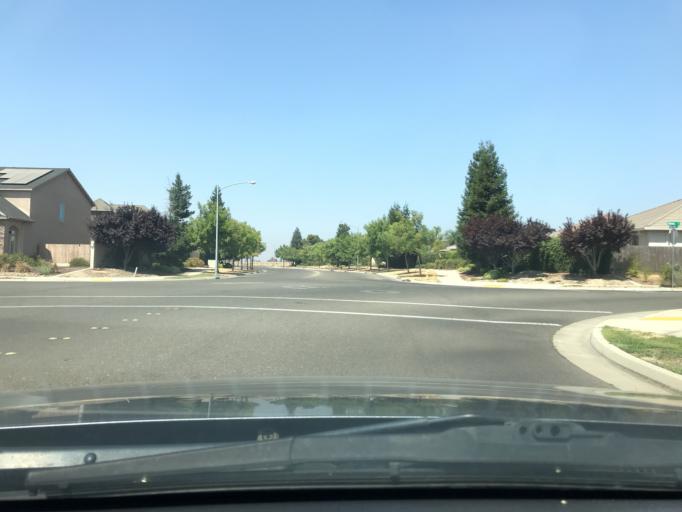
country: US
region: California
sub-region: Merced County
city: Merced
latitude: 37.3579
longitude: -120.4705
